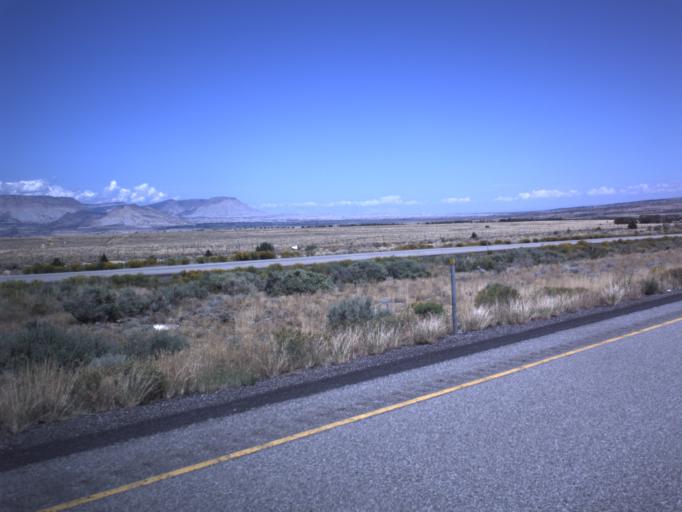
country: US
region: Utah
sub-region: Emery County
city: Ferron
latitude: 38.7781
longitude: -111.3161
